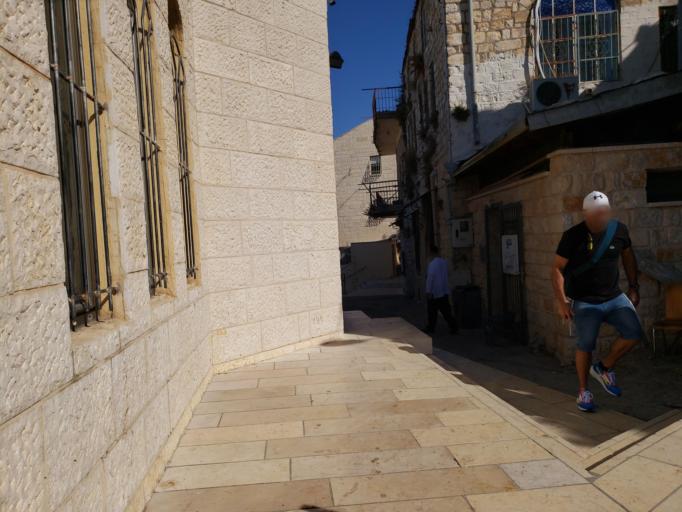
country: IL
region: Northern District
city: Safed
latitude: 32.9684
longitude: 35.4908
